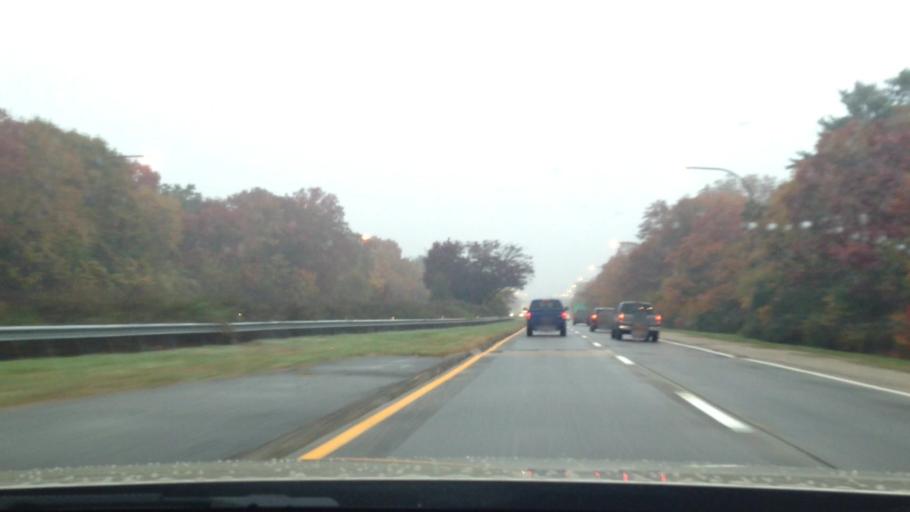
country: US
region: New York
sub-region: Suffolk County
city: Bay Wood
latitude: 40.7645
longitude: -73.2798
